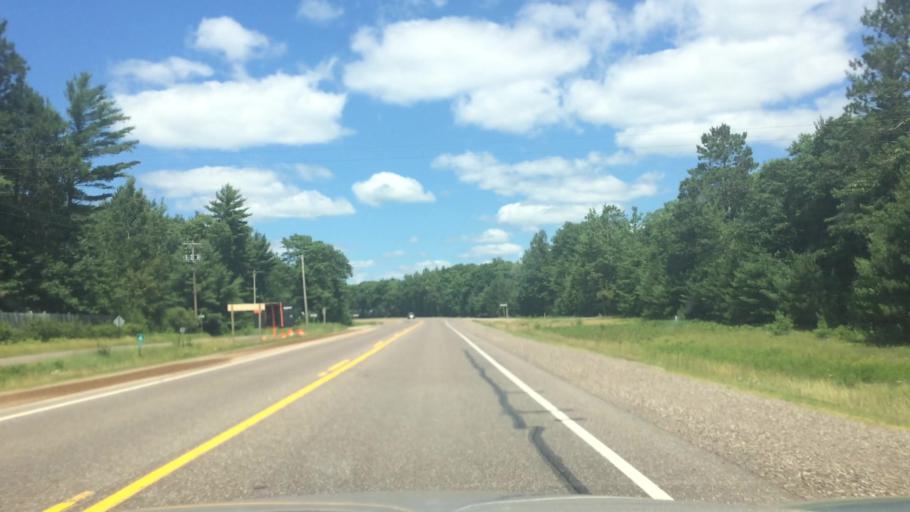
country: US
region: Wisconsin
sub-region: Vilas County
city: Lac du Flambeau
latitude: 45.9387
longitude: -89.6965
